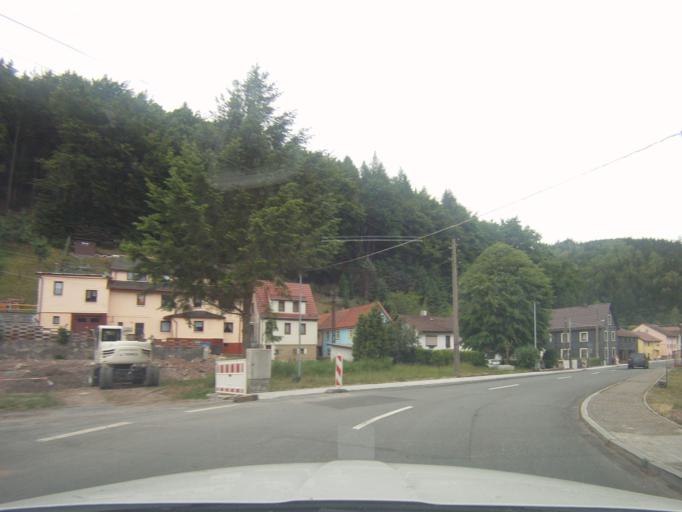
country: DE
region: Thuringia
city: Frauenwald
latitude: 50.5053
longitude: 10.8462
